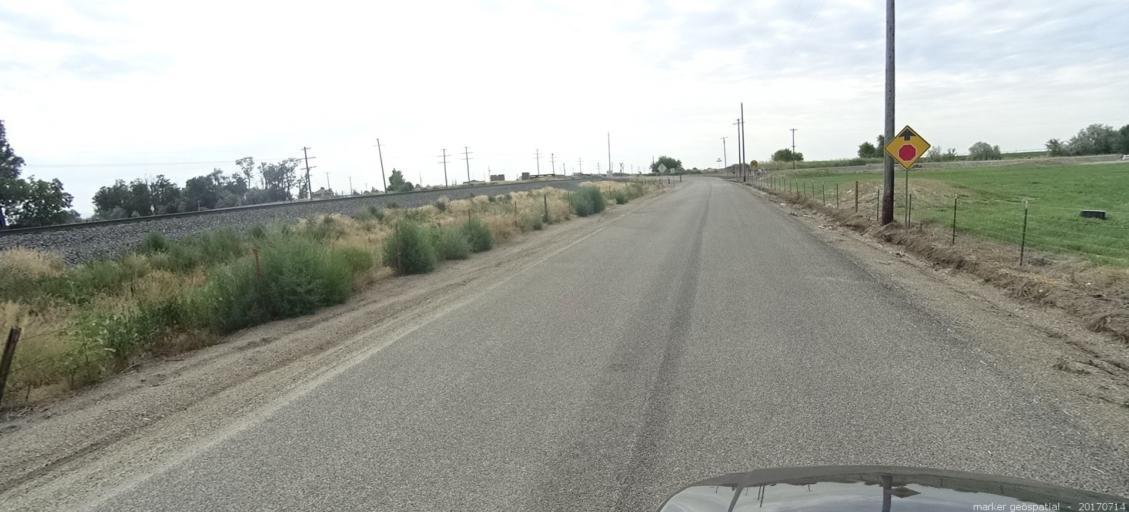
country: US
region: Idaho
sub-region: Ada County
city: Kuna
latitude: 43.4591
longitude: -116.3560
